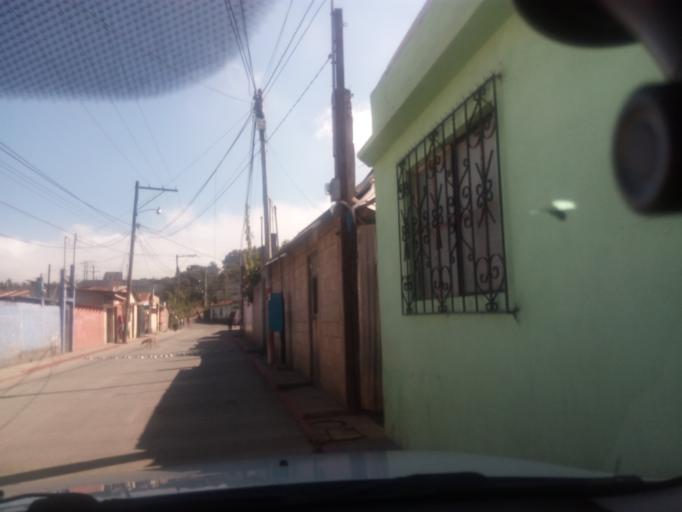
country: GT
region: Sacatepequez
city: San Bartolome Milpas Altas
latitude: 14.6046
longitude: -90.6779
